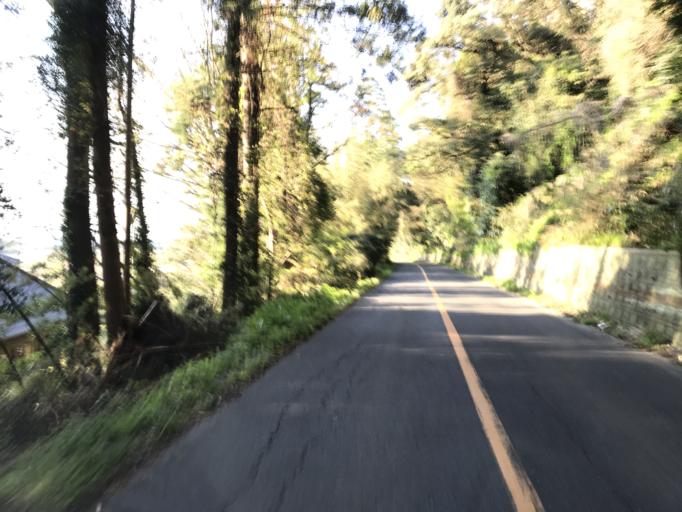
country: JP
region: Chiba
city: Yokaichiba
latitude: 35.7201
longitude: 140.5636
